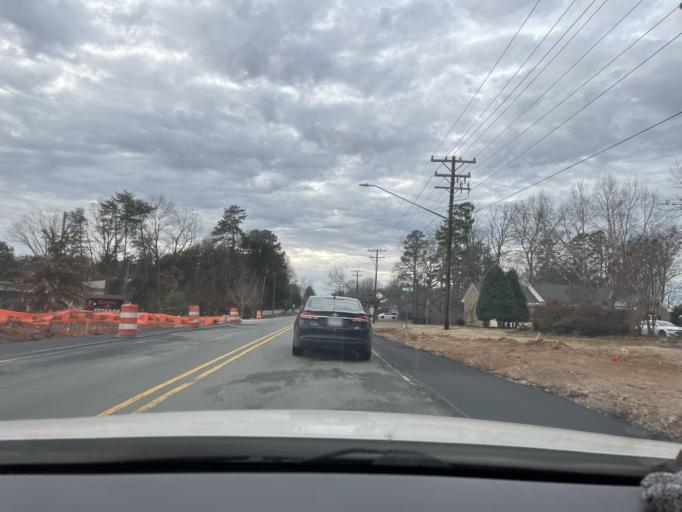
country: US
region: North Carolina
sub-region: Alamance County
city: Elon
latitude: 36.0738
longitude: -79.5086
